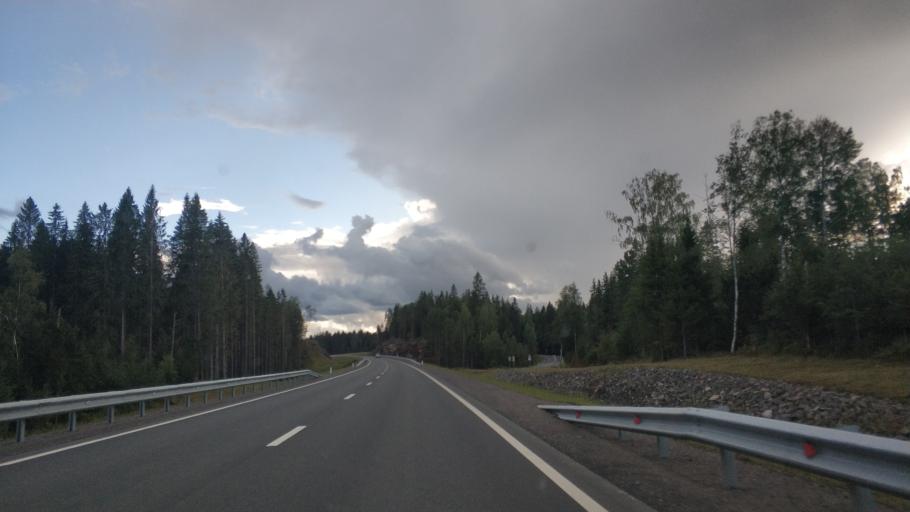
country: RU
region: Republic of Karelia
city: Lakhdenpokh'ya
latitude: 61.4270
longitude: 29.9679
